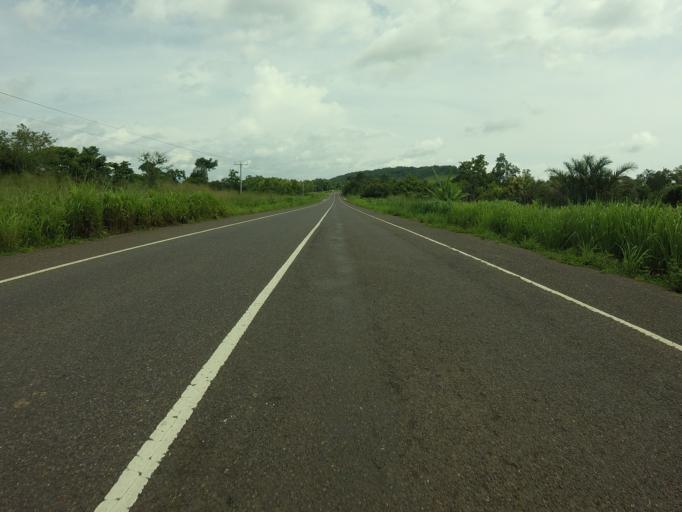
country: TG
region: Plateaux
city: Badou
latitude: 7.9514
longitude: 0.5544
